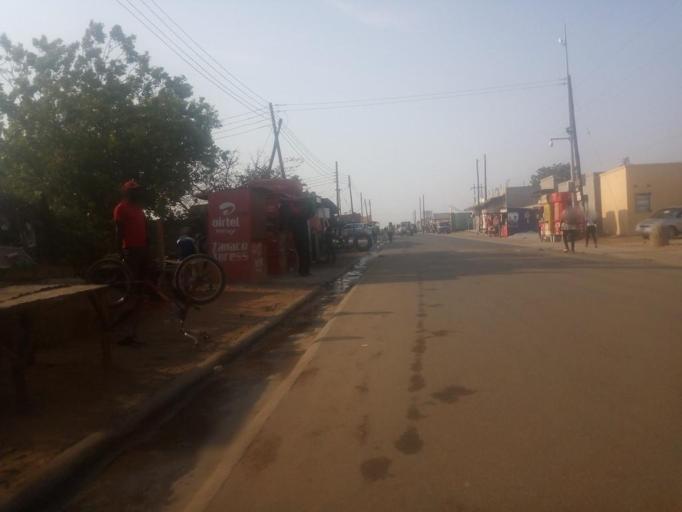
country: ZM
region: Lusaka
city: Lusaka
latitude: -15.4054
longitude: 28.3698
